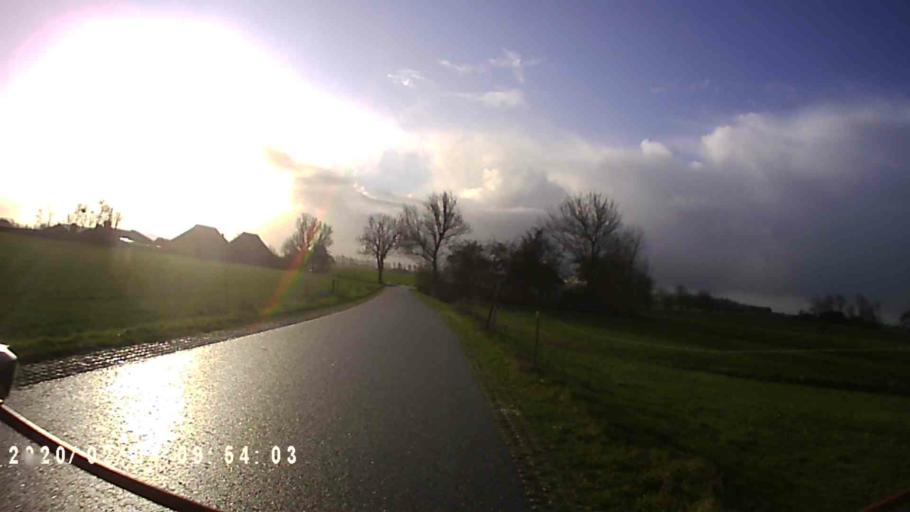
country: NL
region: Groningen
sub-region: Gemeente Zuidhorn
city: Aduard
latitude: 53.2792
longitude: 6.4984
